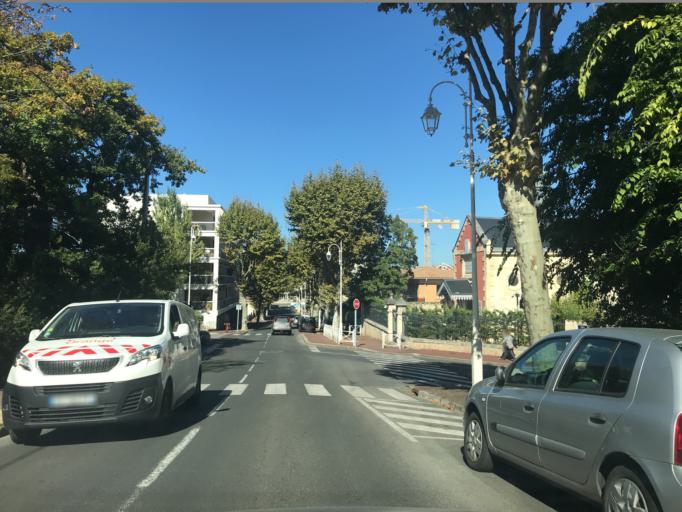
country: FR
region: Aquitaine
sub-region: Departement de la Gironde
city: Arcachon
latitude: 44.6574
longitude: -1.1681
